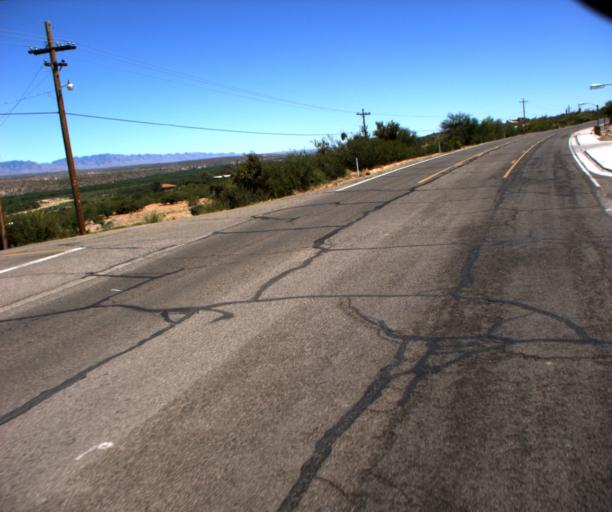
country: US
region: Arizona
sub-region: Pinal County
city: Mammoth
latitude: 32.7159
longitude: -110.6421
